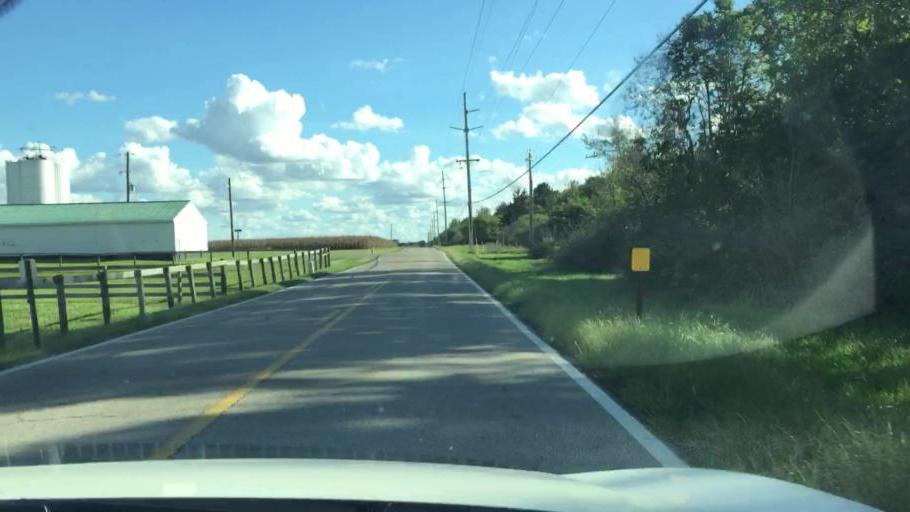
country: US
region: Ohio
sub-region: Clark County
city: Northridge
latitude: 39.9625
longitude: -83.7081
